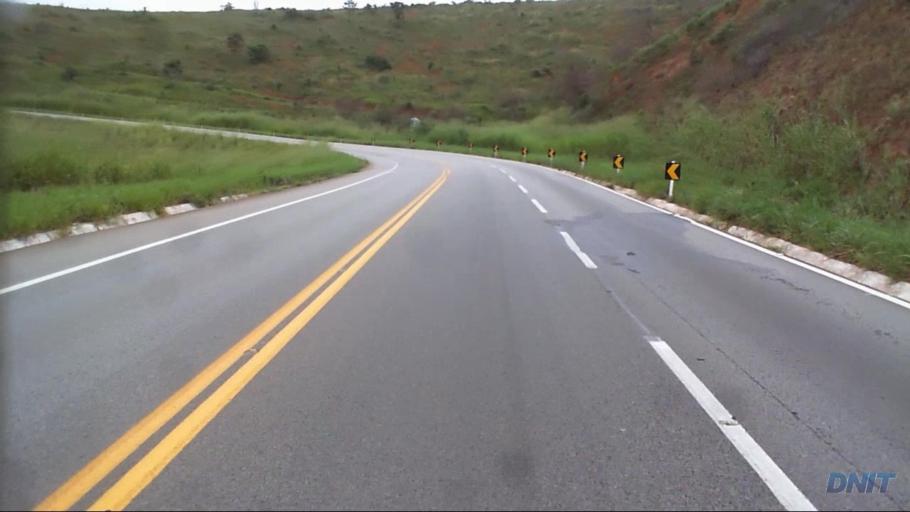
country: BR
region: Minas Gerais
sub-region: Nova Era
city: Nova Era
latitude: -19.7932
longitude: -43.0557
